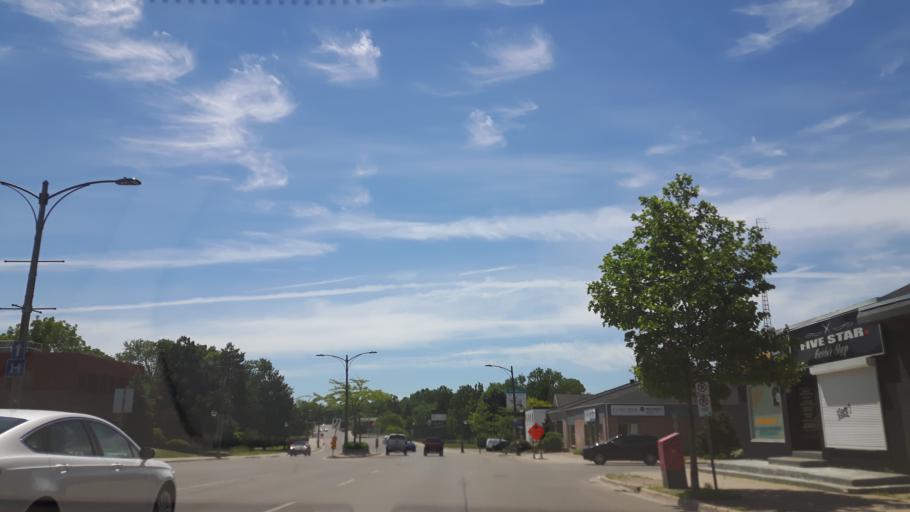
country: CA
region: Ontario
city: London
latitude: 42.9758
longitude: -81.2409
